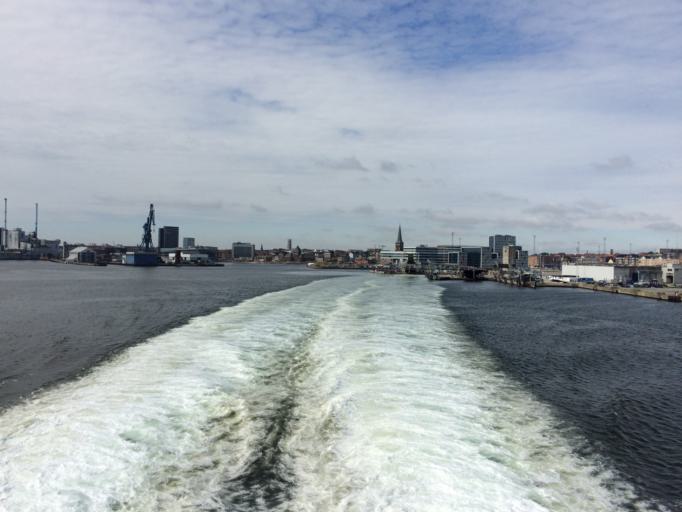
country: DK
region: Central Jutland
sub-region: Arhus Kommune
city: Arhus
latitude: 56.1614
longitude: 10.2302
